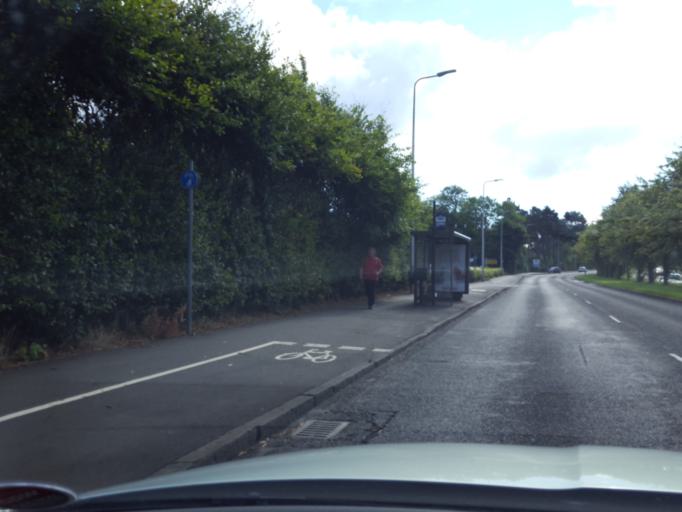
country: GB
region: Scotland
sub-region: Fife
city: Rosyth
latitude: 56.0544
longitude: -3.4366
